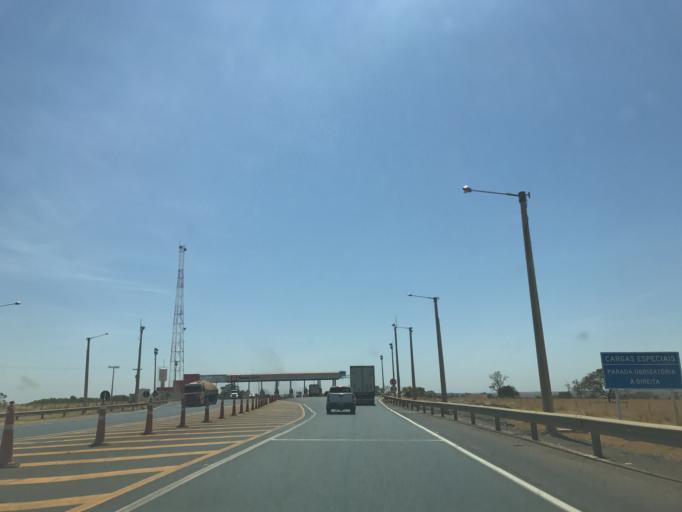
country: BR
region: Minas Gerais
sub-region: Prata
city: Prata
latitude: -19.4733
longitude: -48.8698
